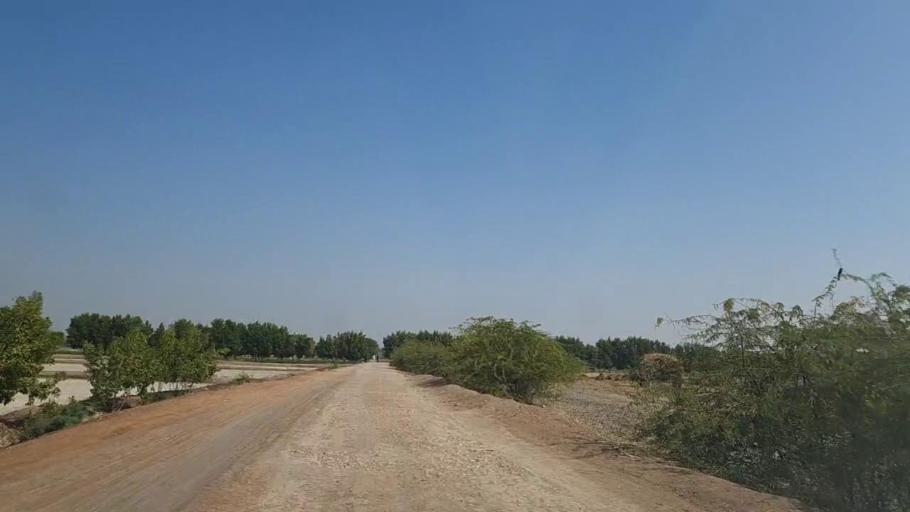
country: PK
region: Sindh
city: Naukot
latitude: 24.8616
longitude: 69.4319
